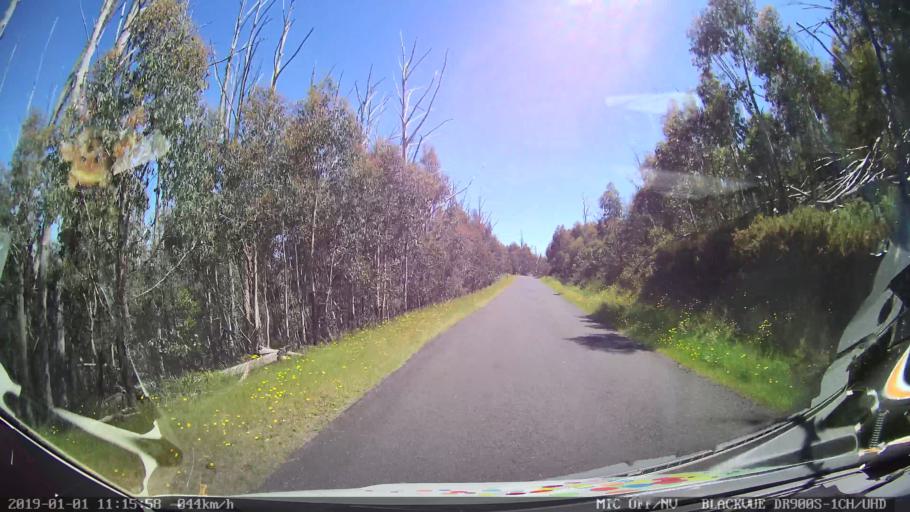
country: AU
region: New South Wales
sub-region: Snowy River
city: Jindabyne
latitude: -35.9419
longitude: 148.3857
